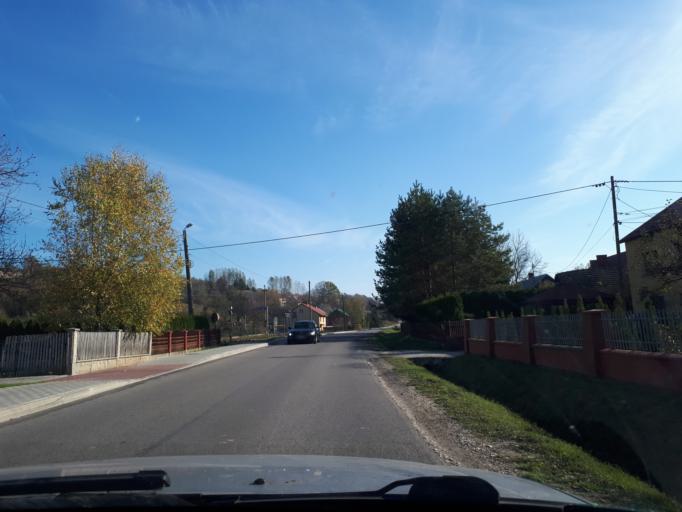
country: PL
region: Subcarpathian Voivodeship
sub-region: Powiat debicki
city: Debica
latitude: 50.0026
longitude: 21.4088
